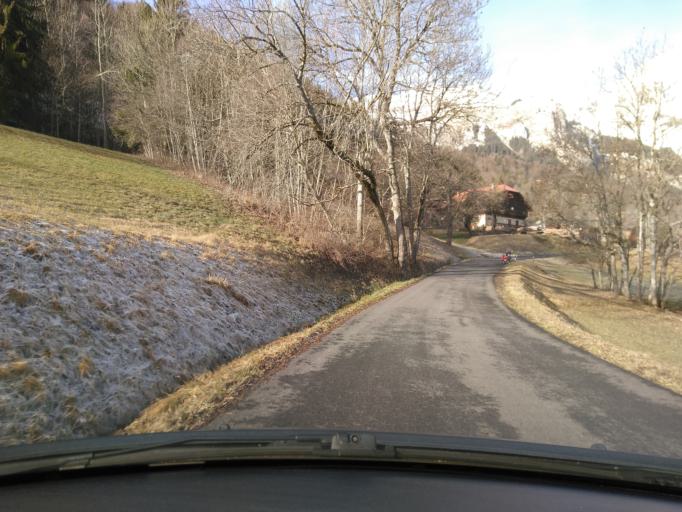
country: FR
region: Rhone-Alpes
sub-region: Departement de la Haute-Savoie
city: Sallanches
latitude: 45.9537
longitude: 6.6148
